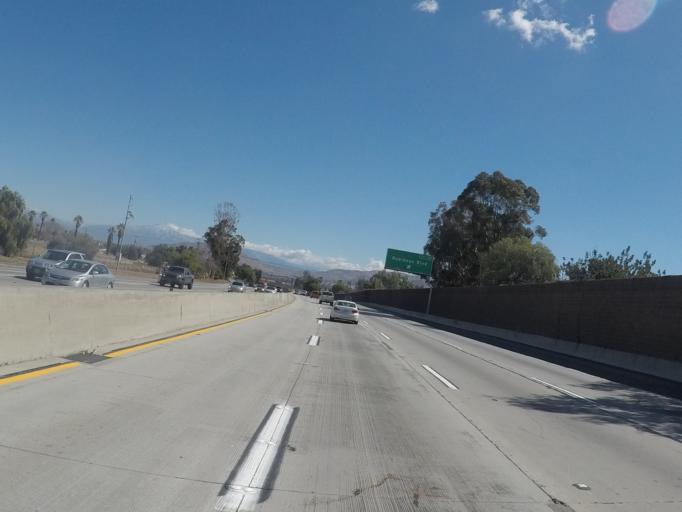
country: US
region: California
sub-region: Riverside County
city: Rubidoux
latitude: 34.0041
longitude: -117.4066
